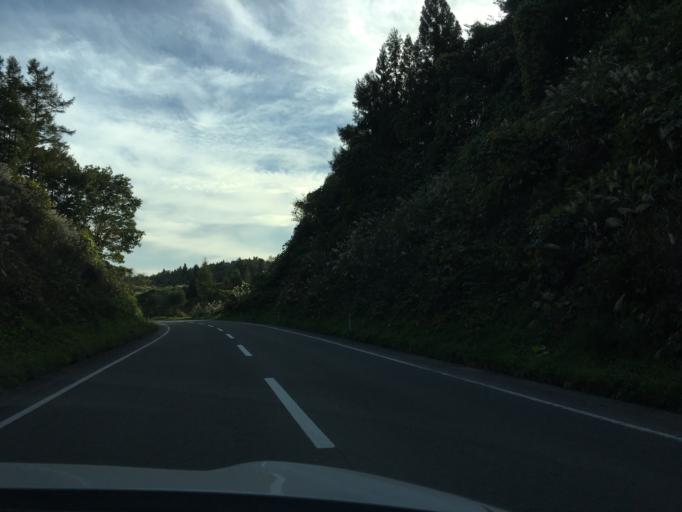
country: JP
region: Fukushima
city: Ishikawa
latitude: 37.2079
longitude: 140.5483
